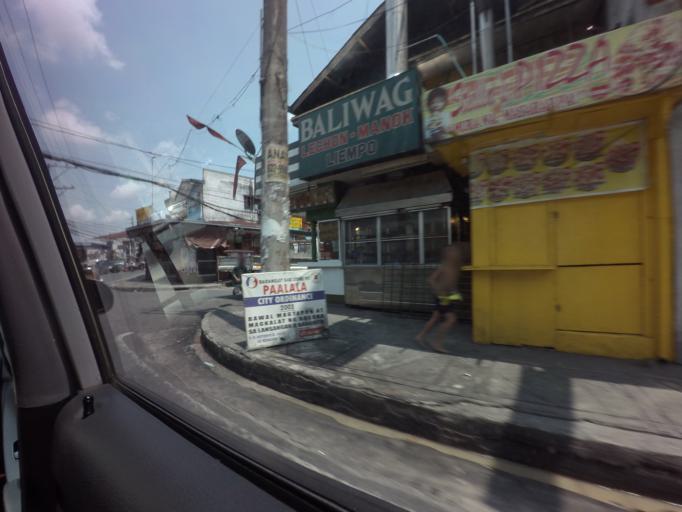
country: PH
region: Metro Manila
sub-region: City of Manila
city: Quiapo
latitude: 14.5927
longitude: 121.0044
